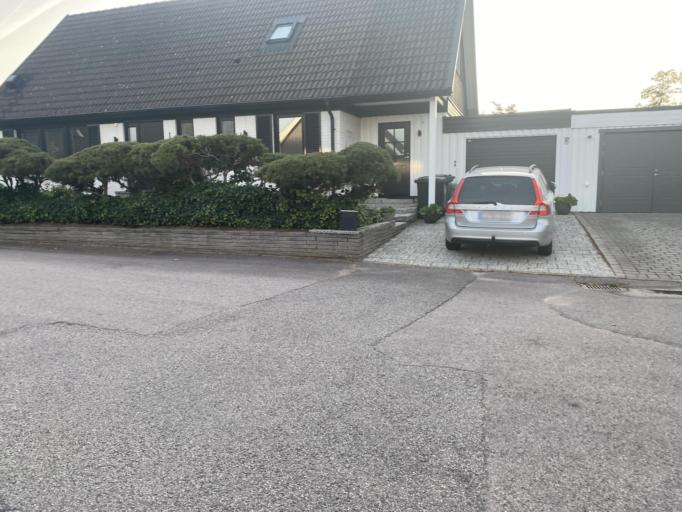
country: SE
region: Kronoberg
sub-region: Vaxjo Kommun
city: Vaexjoe
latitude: 56.9131
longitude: 14.7837
